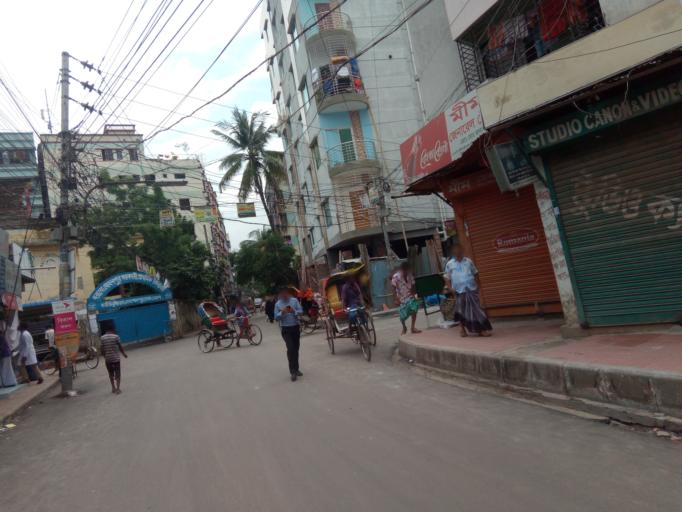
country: BD
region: Dhaka
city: Azimpur
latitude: 23.7682
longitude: 90.3618
